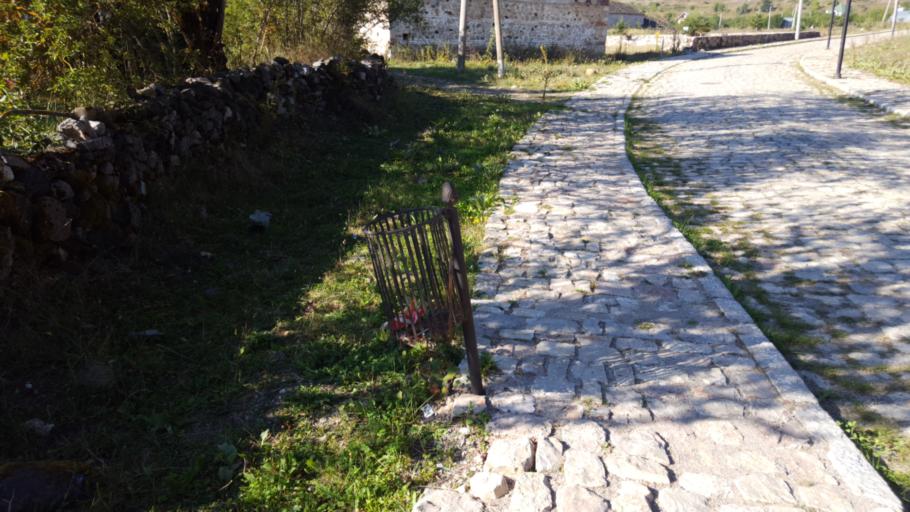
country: AL
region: Korce
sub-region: Rrethi i Korces
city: Voskopoje
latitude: 40.6304
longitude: 20.5885
